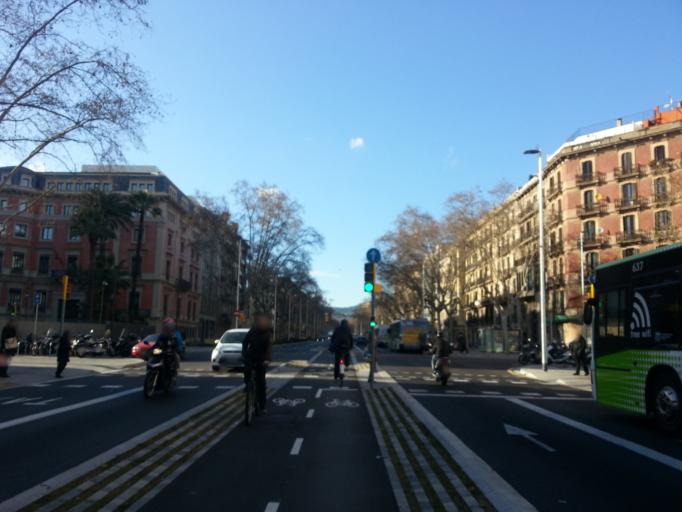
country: ES
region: Catalonia
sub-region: Provincia de Barcelona
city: Eixample
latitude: 41.3956
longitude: 2.1746
